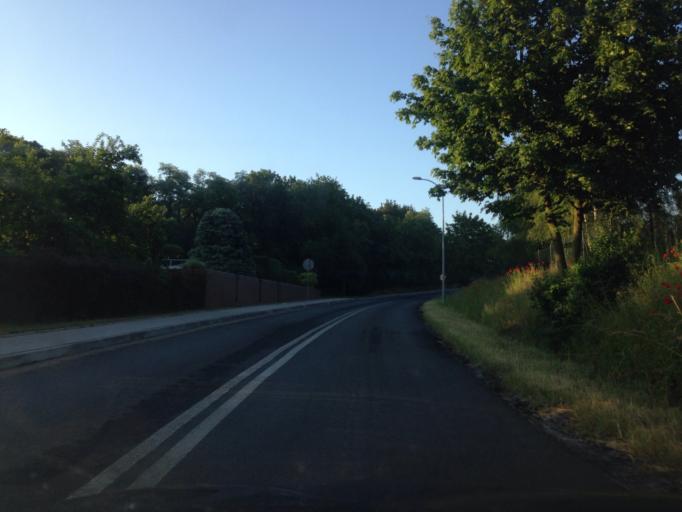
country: PL
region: Pomeranian Voivodeship
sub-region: Powiat tczewski
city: Gniew
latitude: 53.8177
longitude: 18.8186
